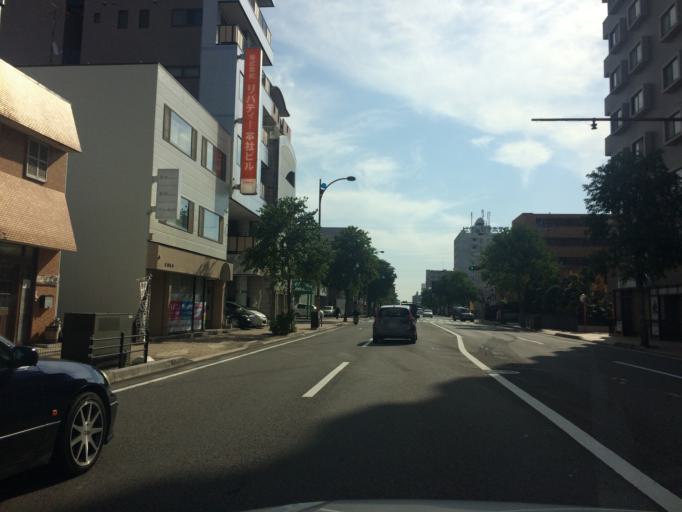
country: JP
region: Shizuoka
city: Shizuoka-shi
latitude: 34.9670
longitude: 138.3938
